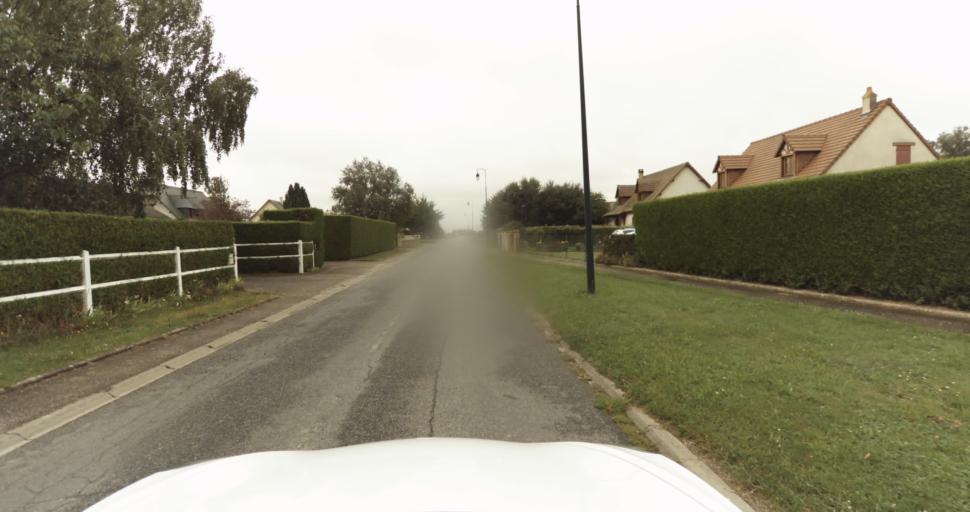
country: FR
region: Haute-Normandie
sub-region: Departement de l'Eure
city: Claville
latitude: 49.0785
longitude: 1.0668
